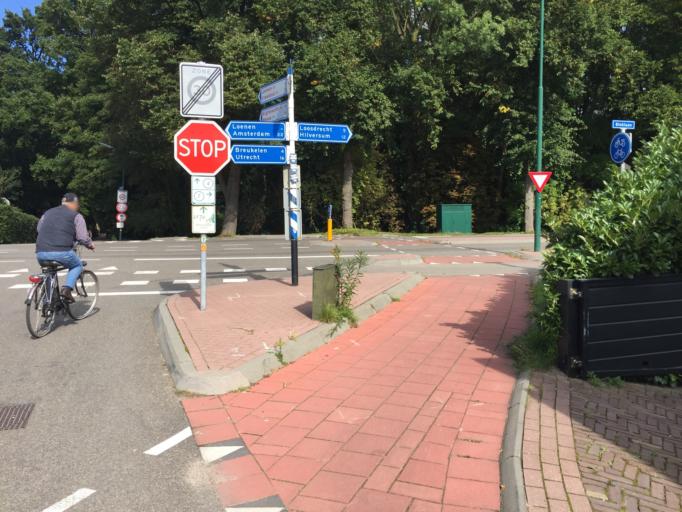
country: NL
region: Utrecht
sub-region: Stichtse Vecht
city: Vreeland
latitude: 52.2043
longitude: 5.0217
